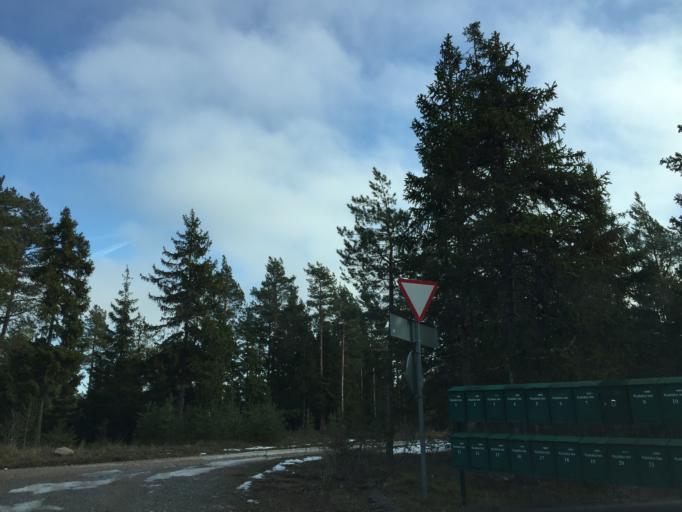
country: EE
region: Saare
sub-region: Kuressaare linn
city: Kuressaare
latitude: 58.4808
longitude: 21.9476
